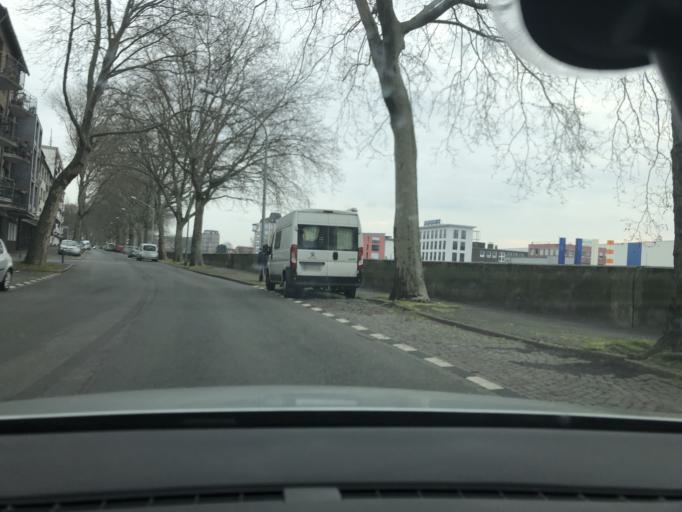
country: DE
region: North Rhine-Westphalia
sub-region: Regierungsbezirk Dusseldorf
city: Duisburg
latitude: 51.4500
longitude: 6.7326
